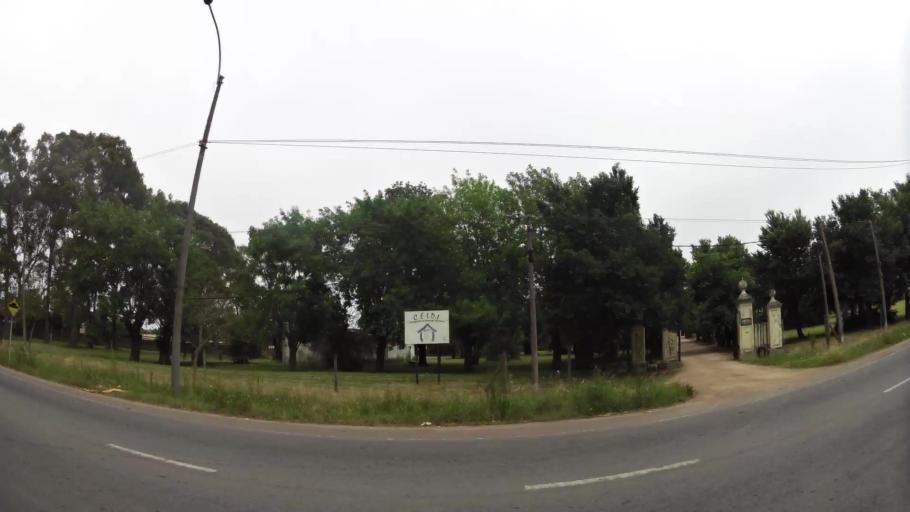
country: UY
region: Canelones
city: La Paz
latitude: -34.7873
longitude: -56.2240
